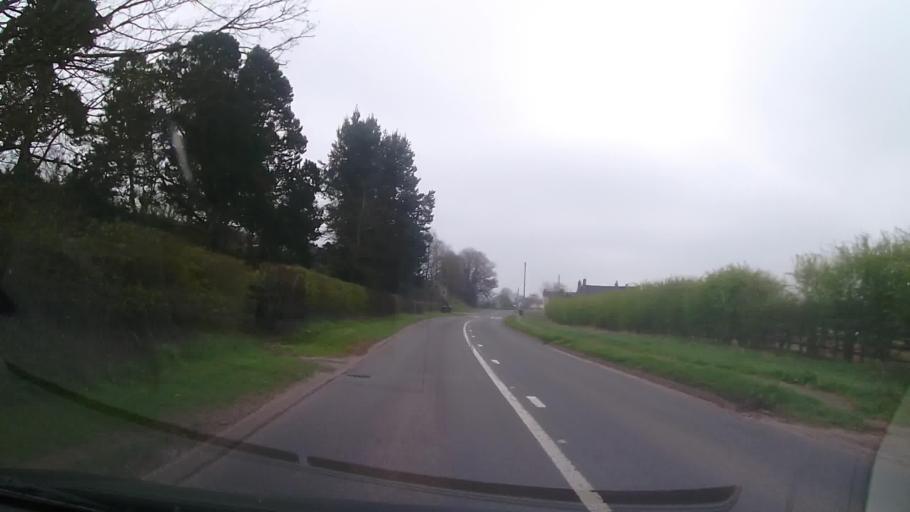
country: GB
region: England
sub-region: Staffordshire
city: Standon
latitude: 52.9481
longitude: -2.3507
